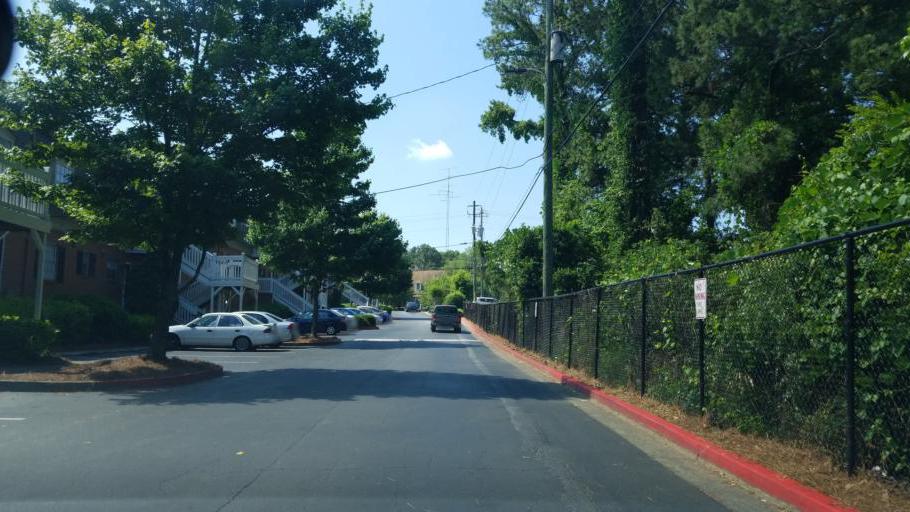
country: US
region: Georgia
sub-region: Cobb County
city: Vinings
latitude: 33.8844
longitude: -84.4825
